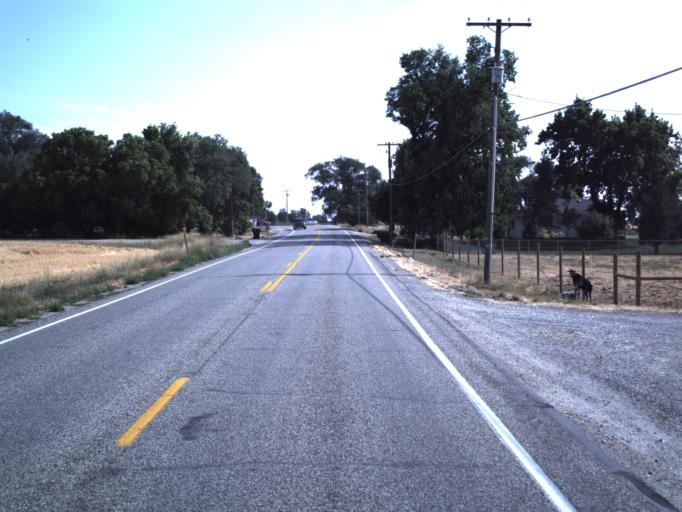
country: US
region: Utah
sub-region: Box Elder County
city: Honeyville
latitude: 41.6720
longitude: -112.0898
